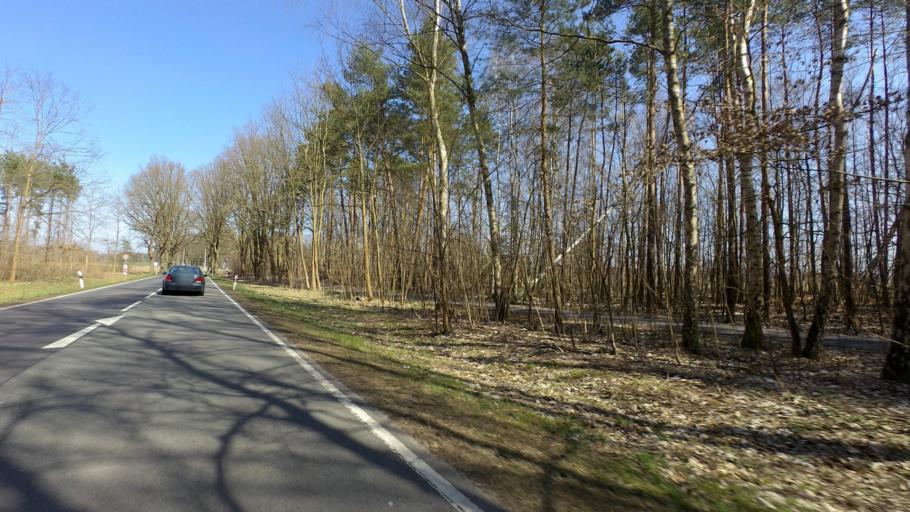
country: DE
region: Brandenburg
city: Lindow
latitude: 52.9476
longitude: 12.9759
